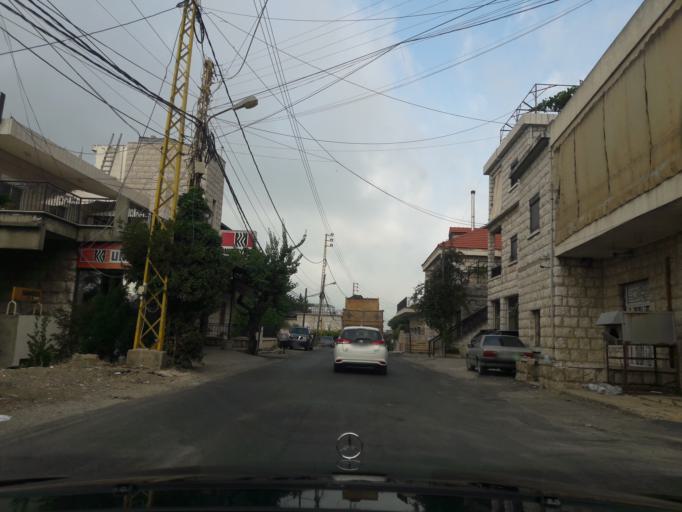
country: LB
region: Mont-Liban
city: Djounie
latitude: 33.9322
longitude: 35.7271
